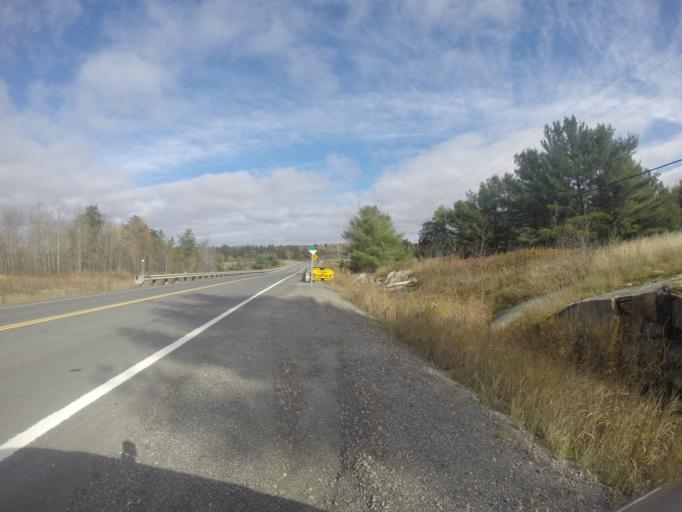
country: CA
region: Ontario
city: Greater Sudbury
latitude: 46.1051
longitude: -80.6550
